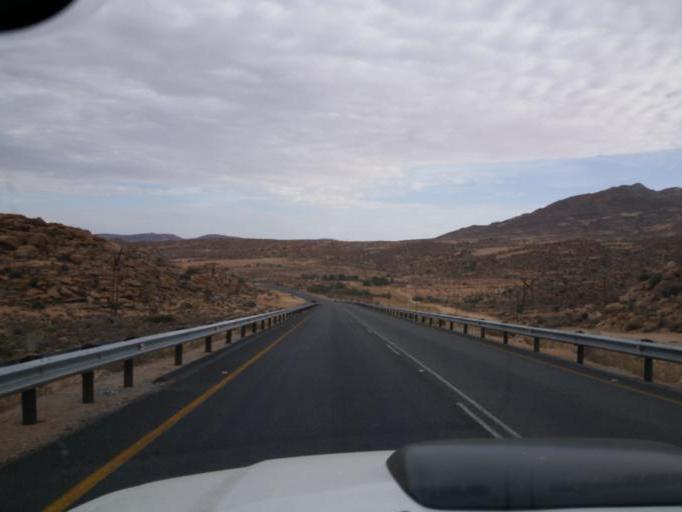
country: ZA
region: Northern Cape
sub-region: Namakwa District Municipality
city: Springbok
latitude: -29.5204
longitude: 17.8595
